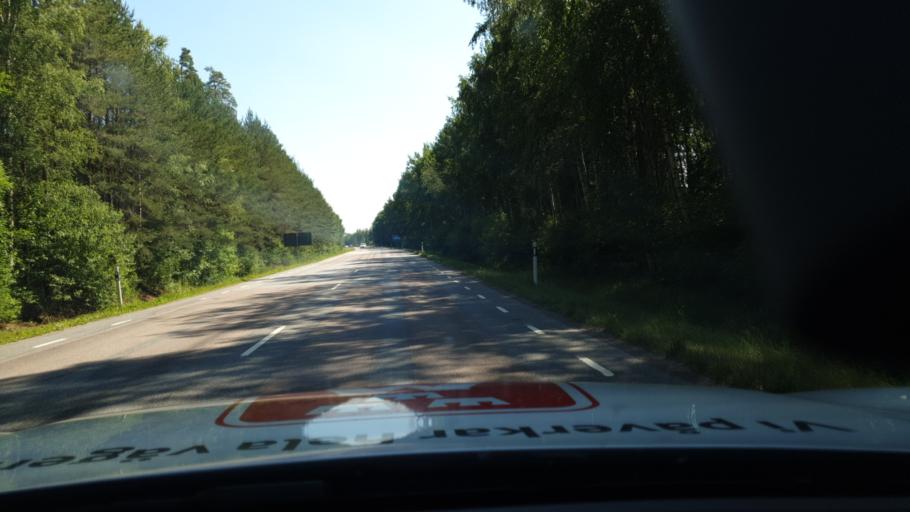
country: SE
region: Vaestra Goetaland
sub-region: Lidkopings Kommun
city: Lidkoping
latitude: 58.5152
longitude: 13.1153
